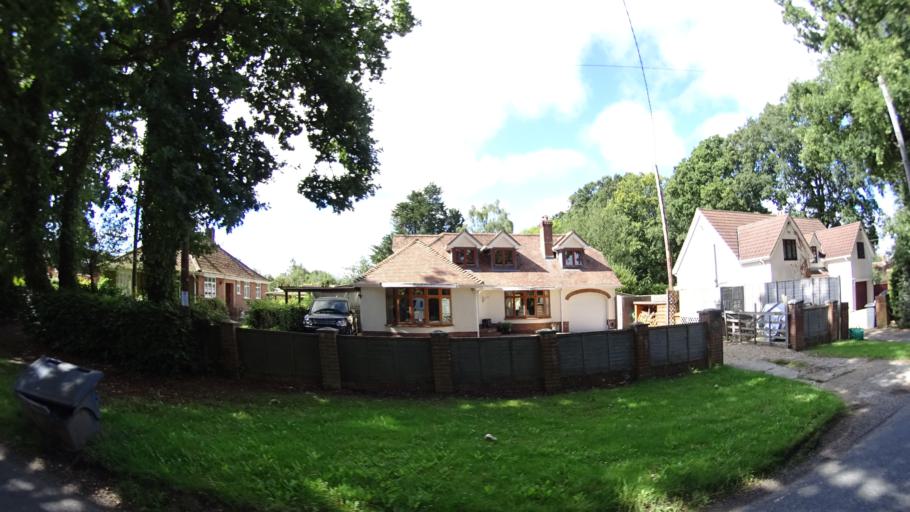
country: GB
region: England
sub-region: Hampshire
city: Romsey
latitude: 51.0113
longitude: -1.4717
